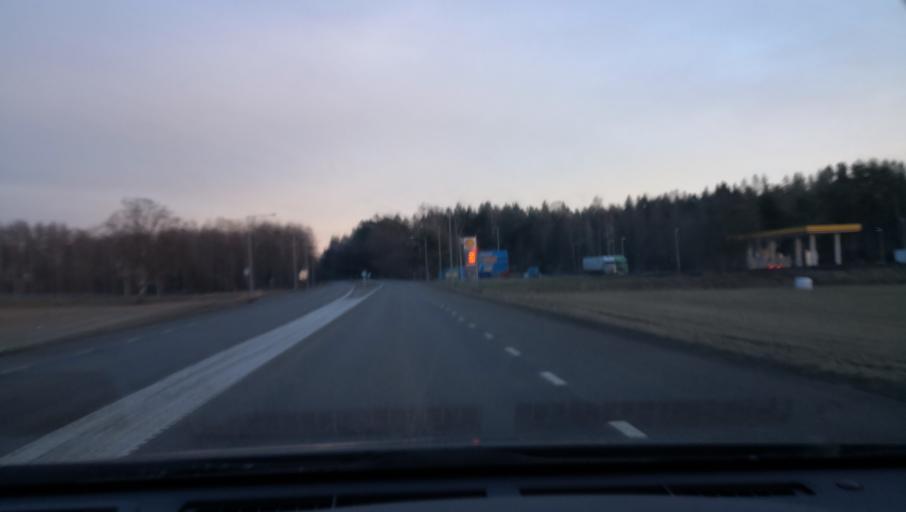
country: SE
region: OErebro
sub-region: Orebro Kommun
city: Vintrosa
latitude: 59.2417
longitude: 15.0267
